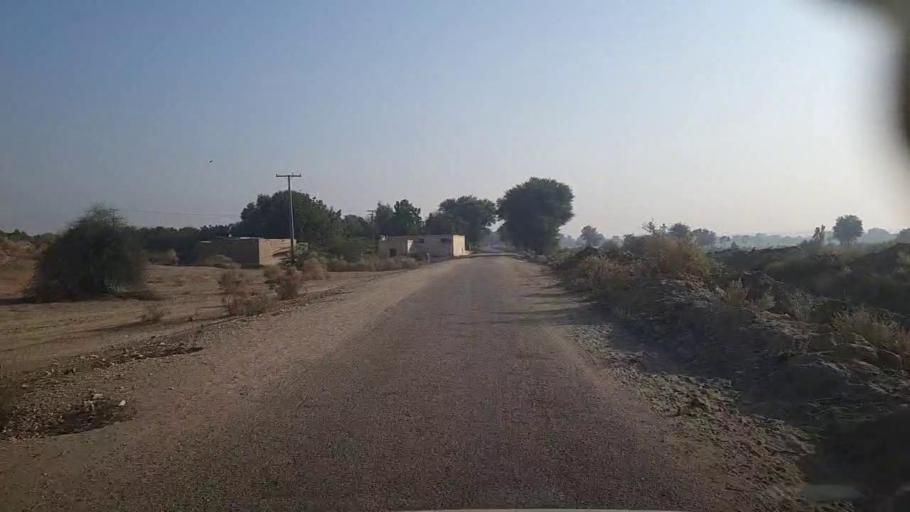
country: PK
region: Sindh
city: Karaundi
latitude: 26.7616
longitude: 68.4757
